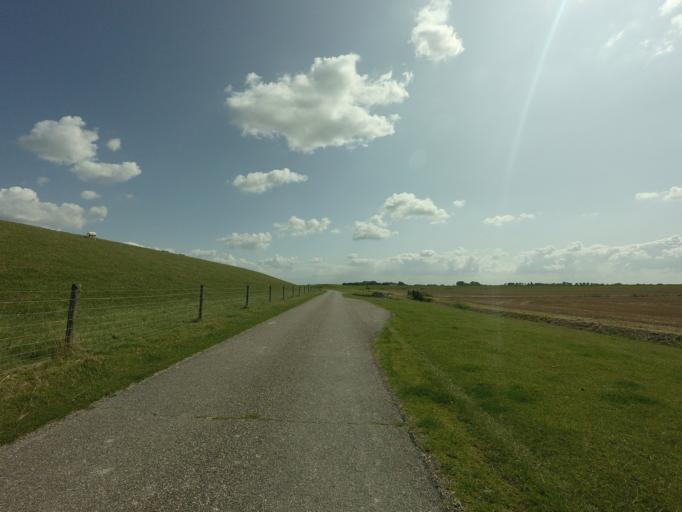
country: NL
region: Friesland
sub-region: Gemeente Ferwerderadiel
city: Hallum
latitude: 53.3199
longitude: 5.7512
